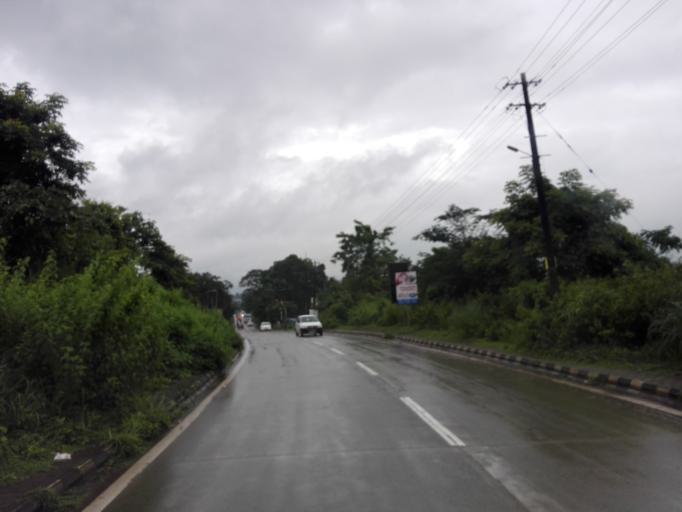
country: IN
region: Kerala
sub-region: Ernakulam
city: Aluva
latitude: 10.0495
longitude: 76.3452
